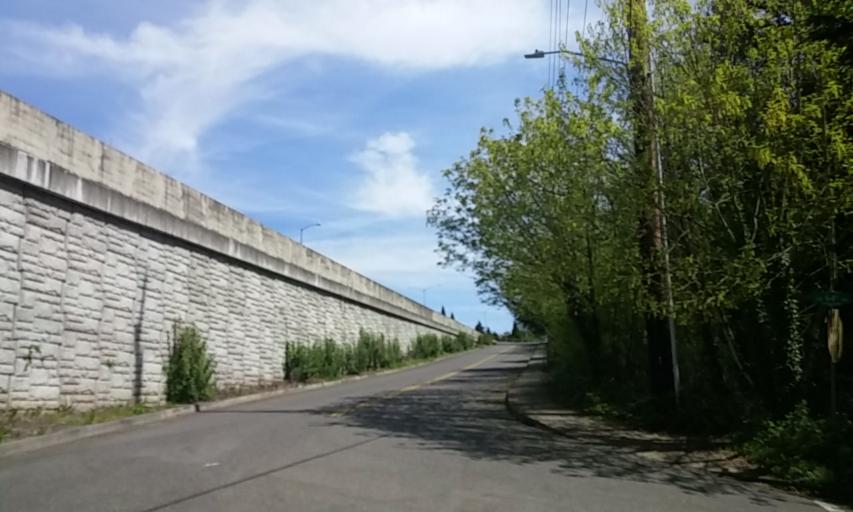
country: US
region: Oregon
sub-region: Washington County
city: West Slope
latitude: 45.5075
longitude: -122.7428
